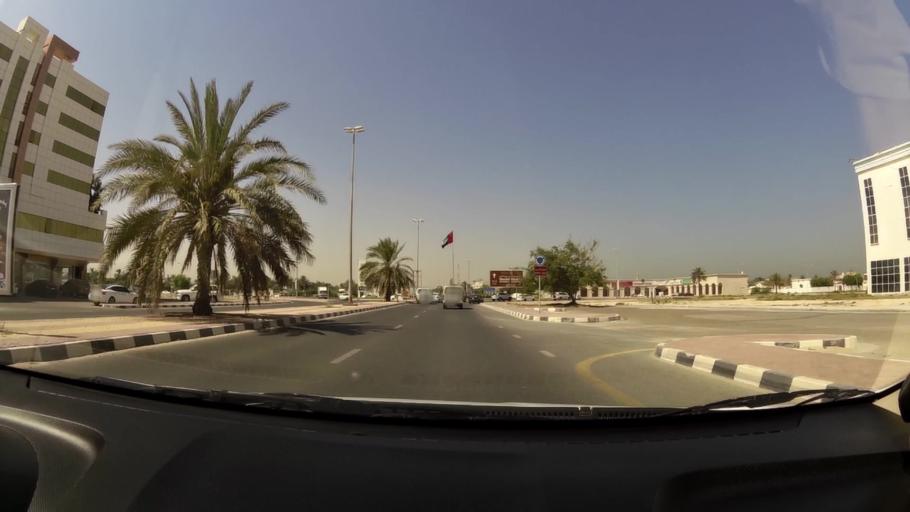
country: AE
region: Umm al Qaywayn
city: Umm al Qaywayn
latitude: 25.5668
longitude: 55.5540
